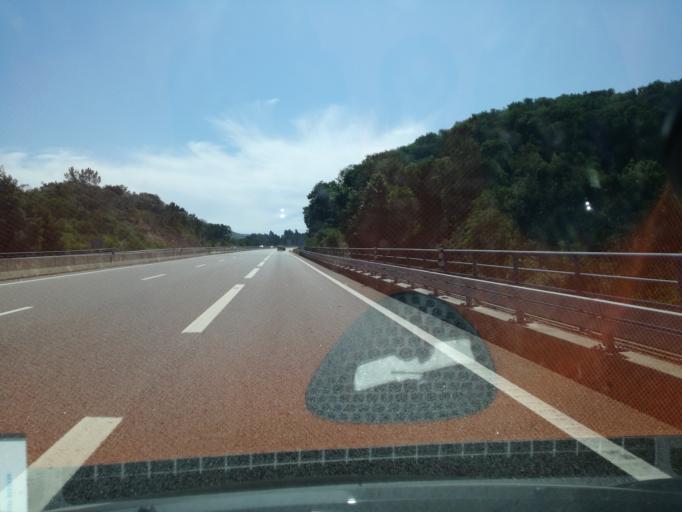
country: PT
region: Viana do Castelo
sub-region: Caminha
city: Vila Praia de Ancora
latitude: 41.7979
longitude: -8.7962
